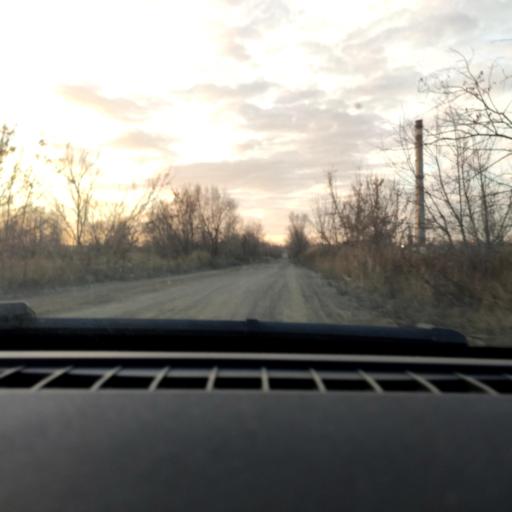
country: RU
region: Voronezj
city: Maslovka
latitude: 51.6130
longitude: 39.2674
